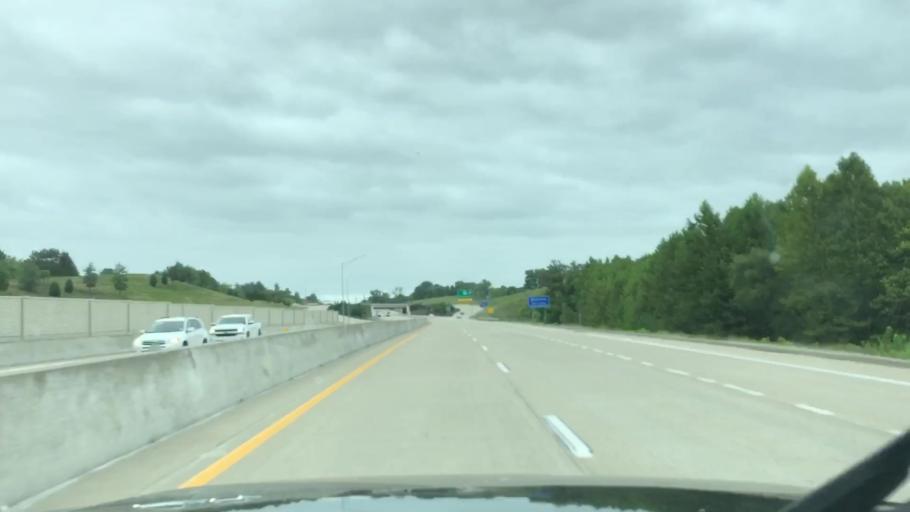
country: US
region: Missouri
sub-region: Saint Louis County
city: Town and Country
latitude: 38.6757
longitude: -90.4935
